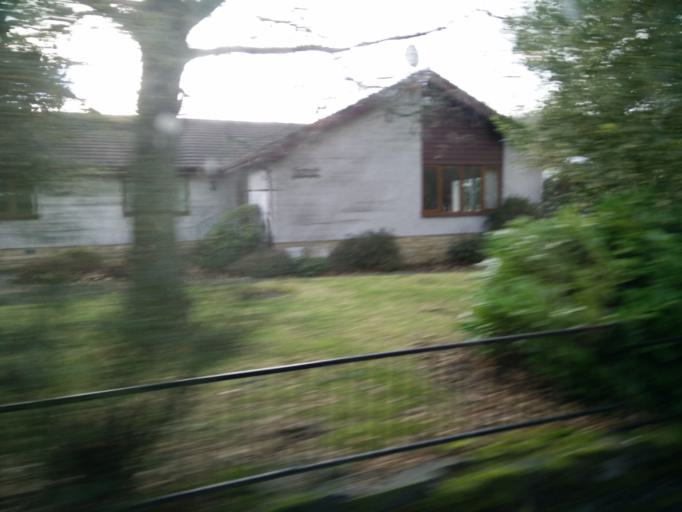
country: GB
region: Scotland
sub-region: Perth and Kinross
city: Aberfeldy
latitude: 56.6181
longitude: -3.8733
